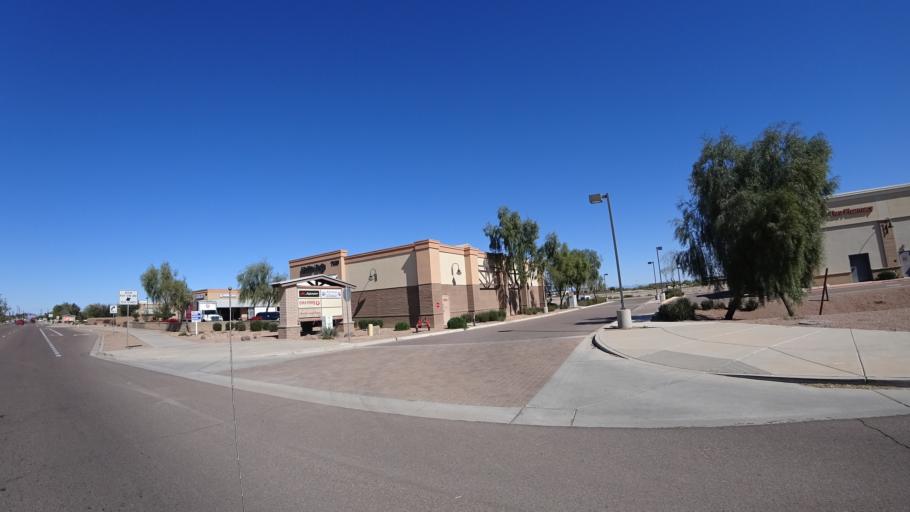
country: US
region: Arizona
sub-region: Maricopa County
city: Queen Creek
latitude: 33.2795
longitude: -111.6861
